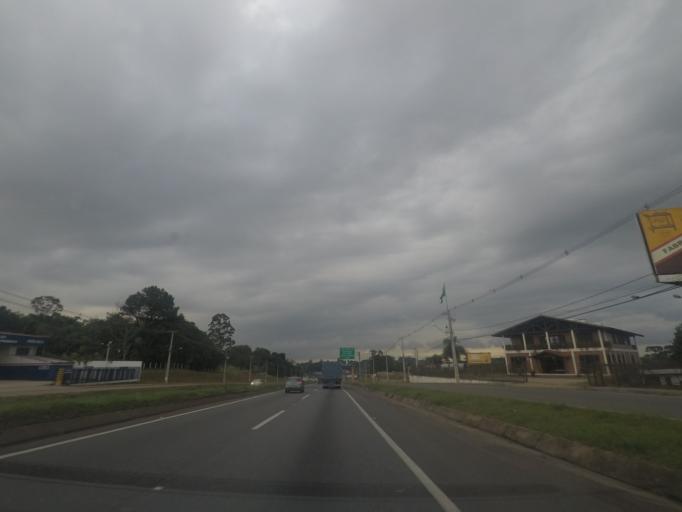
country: BR
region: Parana
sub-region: Sao Jose Dos Pinhais
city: Sao Jose dos Pinhais
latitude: -25.5816
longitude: -49.1774
